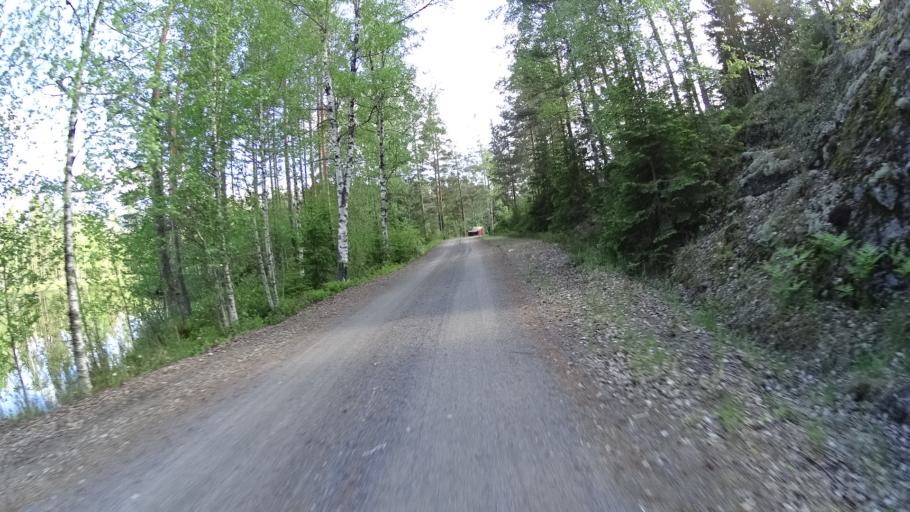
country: FI
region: Varsinais-Suomi
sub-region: Salo
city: Kisko
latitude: 60.1656
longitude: 23.4914
